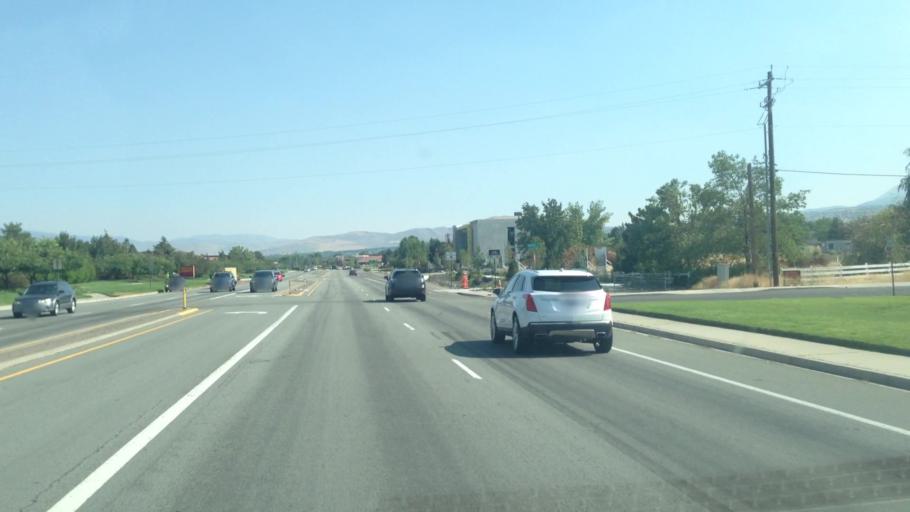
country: US
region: Nevada
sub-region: Washoe County
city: Reno
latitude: 39.4726
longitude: -119.7926
